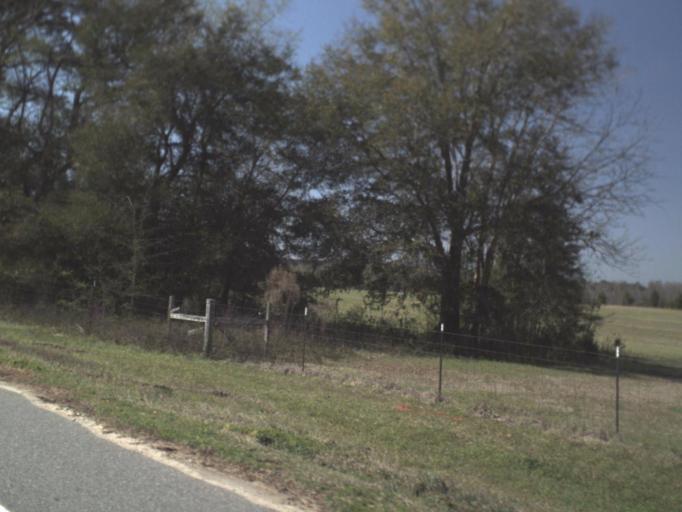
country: US
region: Florida
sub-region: Jackson County
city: Sneads
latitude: 30.6741
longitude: -85.0382
